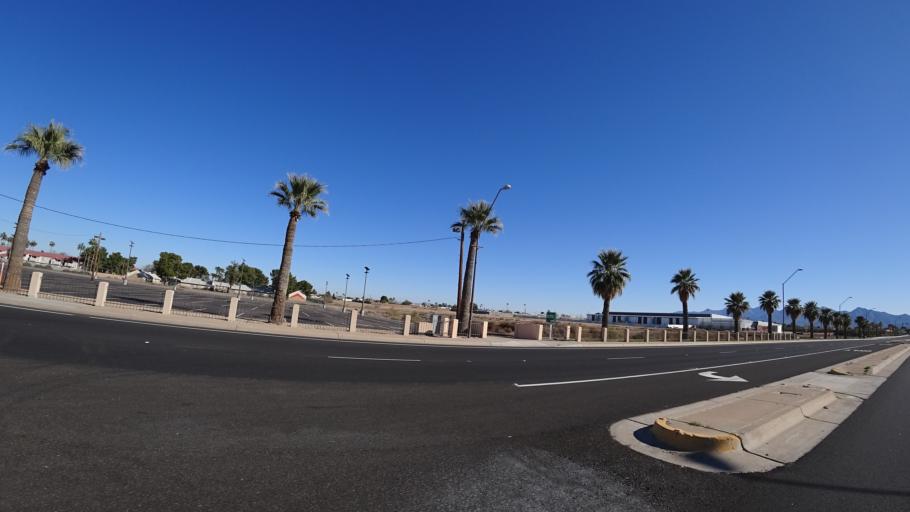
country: US
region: Arizona
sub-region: Maricopa County
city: Goodyear
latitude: 33.4320
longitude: -112.3582
